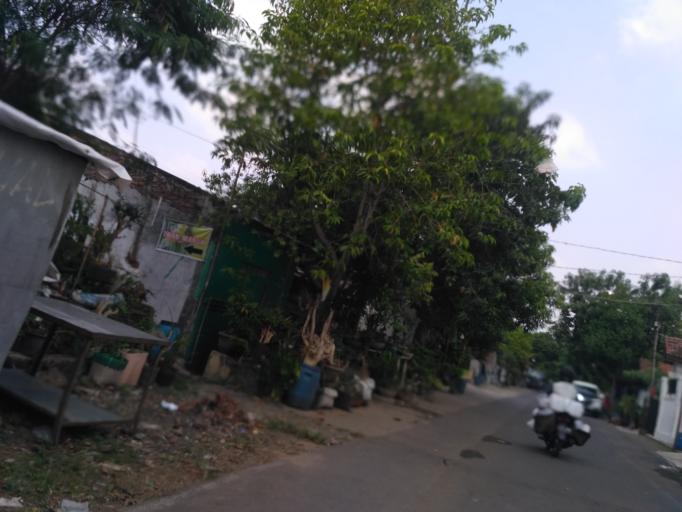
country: ID
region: Central Java
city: Semarang
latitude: -7.0087
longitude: 110.4412
